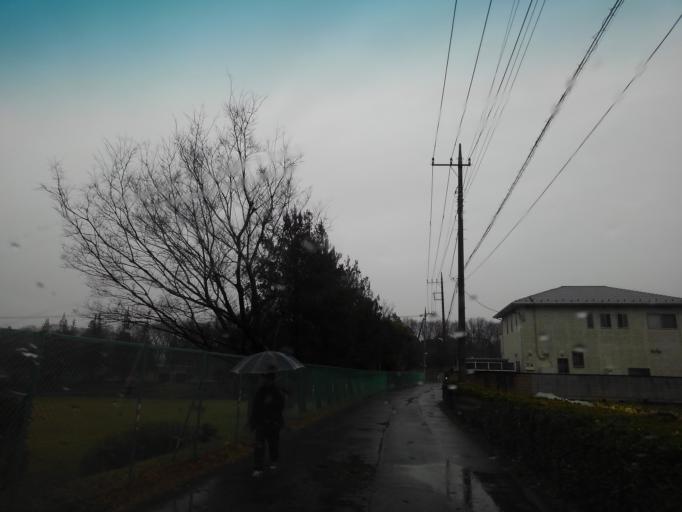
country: JP
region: Saitama
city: Tokorozawa
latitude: 35.8033
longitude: 139.4296
